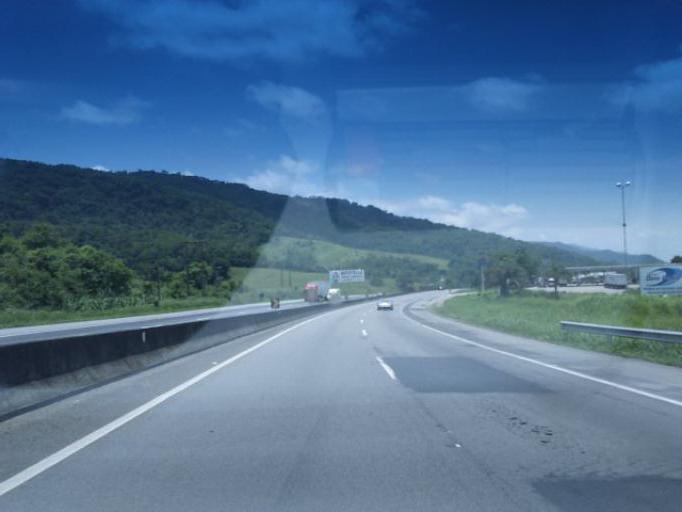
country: BR
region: Sao Paulo
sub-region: Miracatu
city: Miracatu
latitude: -24.3015
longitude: -47.4853
